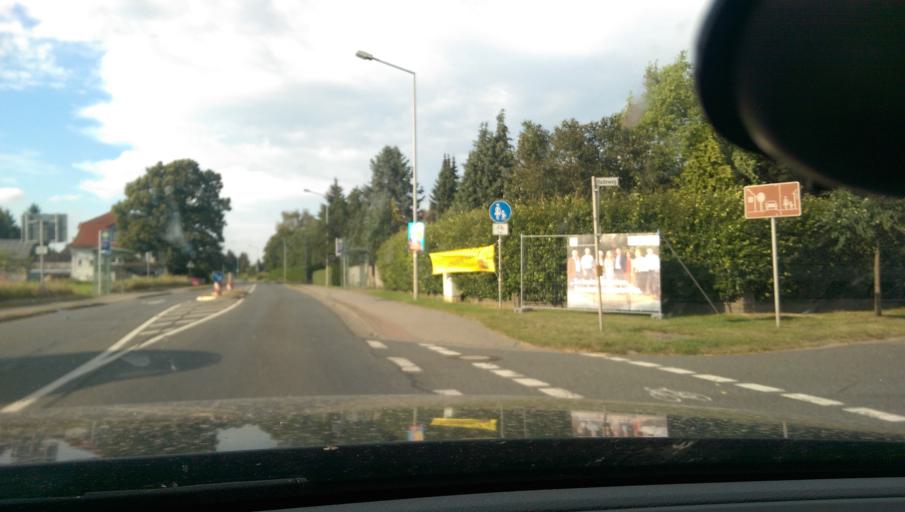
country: DE
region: Lower Saxony
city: Neustadt am Rubenberge
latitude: 52.4862
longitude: 9.4567
